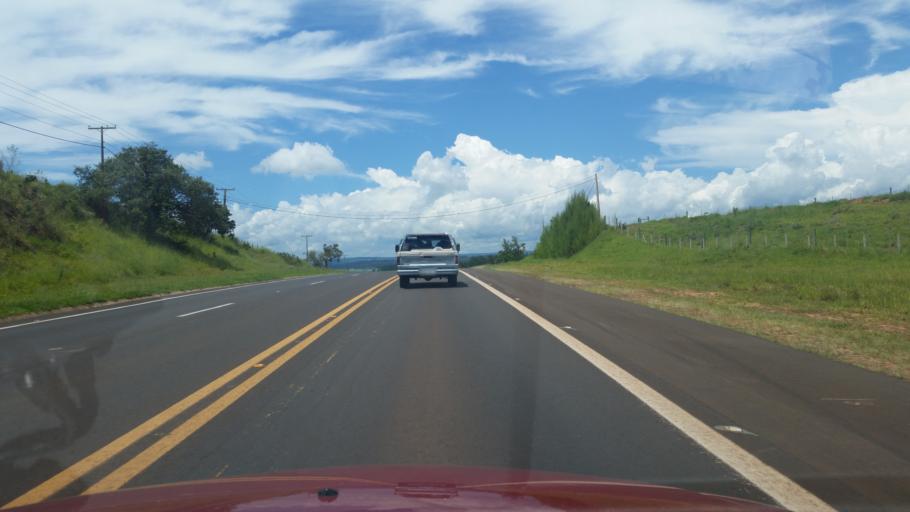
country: BR
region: Sao Paulo
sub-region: Itai
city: Itai
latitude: -23.2833
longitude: -49.0287
